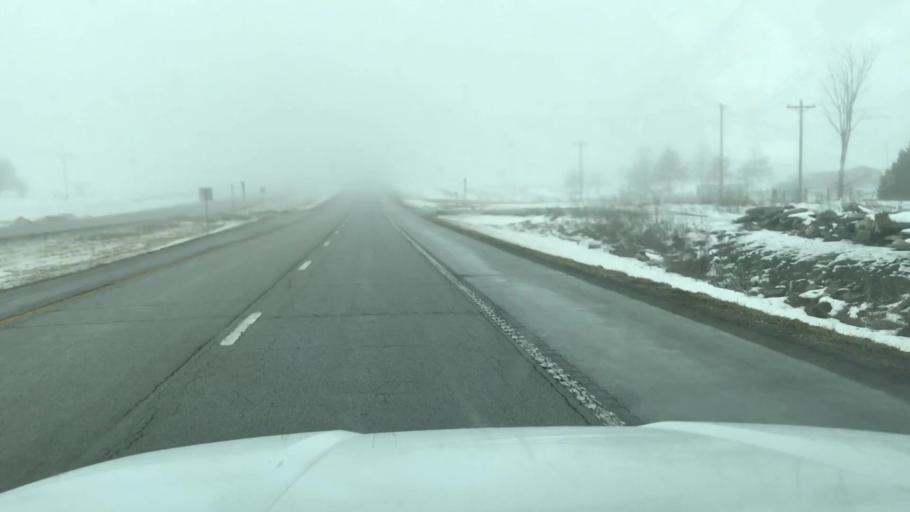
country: US
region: Missouri
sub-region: Clinton County
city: Cameron
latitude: 39.7549
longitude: -94.3180
